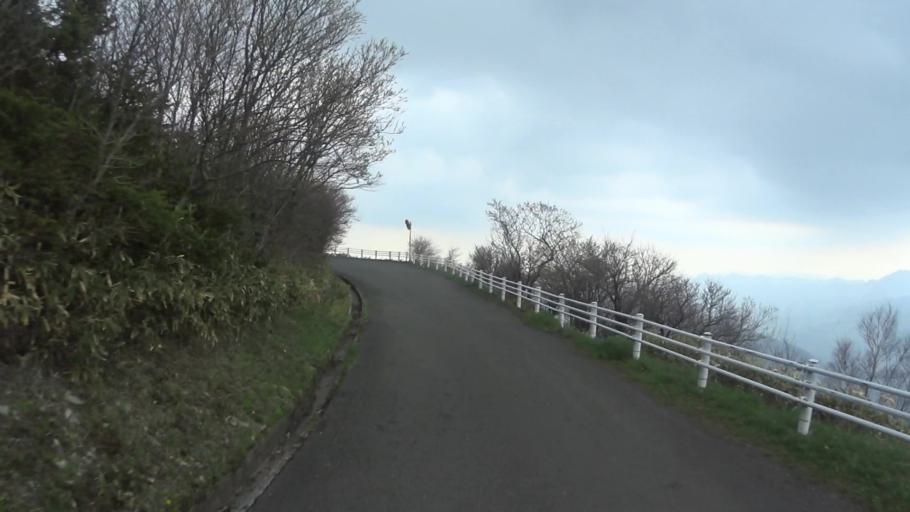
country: JP
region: Ehime
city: Saijo
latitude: 33.7792
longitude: 133.2186
